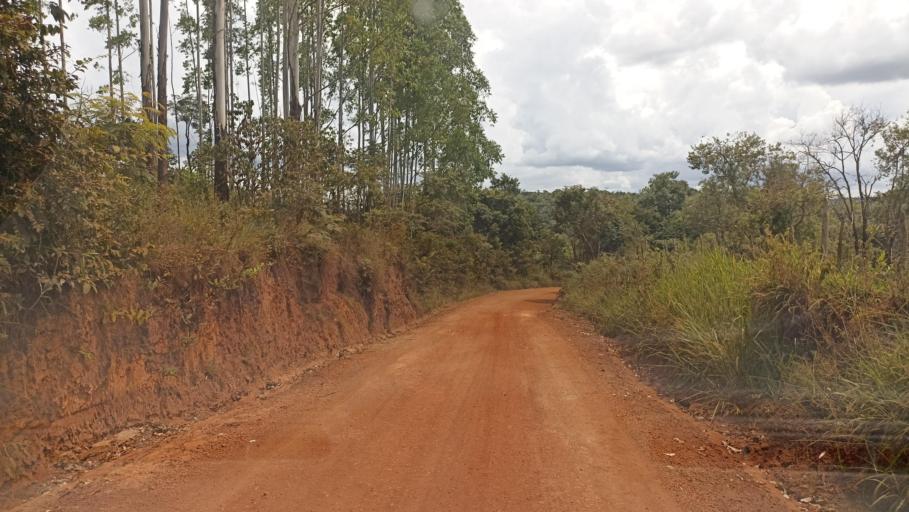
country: BR
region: Minas Gerais
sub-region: Itabirito
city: Itabirito
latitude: -20.3538
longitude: -43.7371
